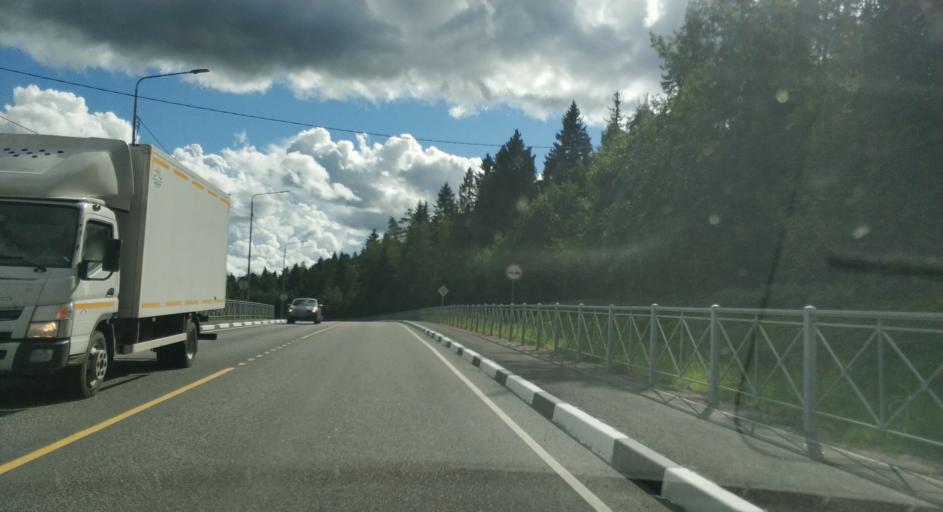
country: RU
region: Republic of Karelia
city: Ruskeala
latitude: 61.9287
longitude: 30.5985
